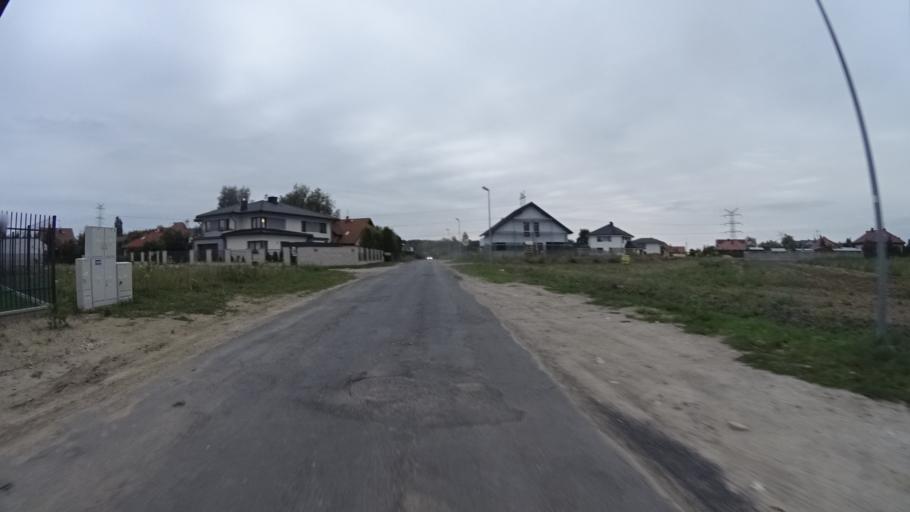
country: PL
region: Masovian Voivodeship
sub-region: Powiat warszawski zachodni
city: Stare Babice
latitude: 52.2582
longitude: 20.8204
